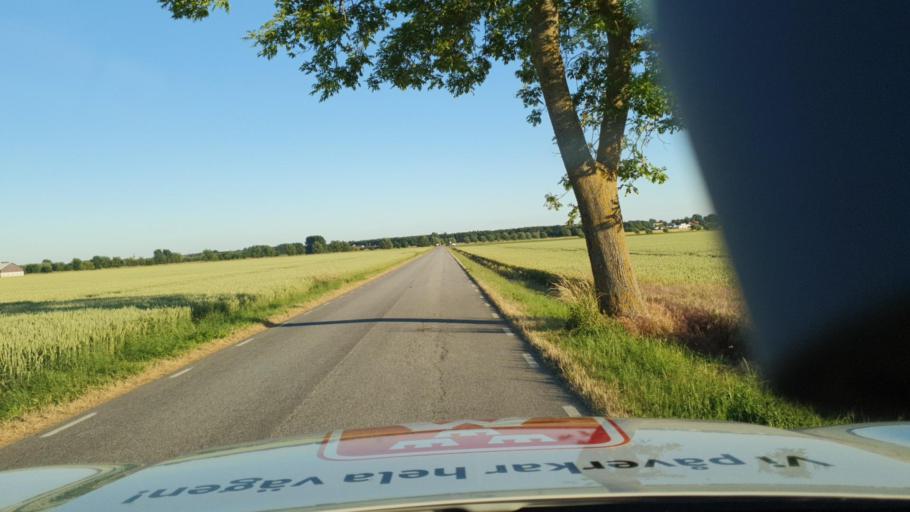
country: SE
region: Skane
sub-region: Lomma Kommun
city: Lomma
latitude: 55.7068
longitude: 13.0594
